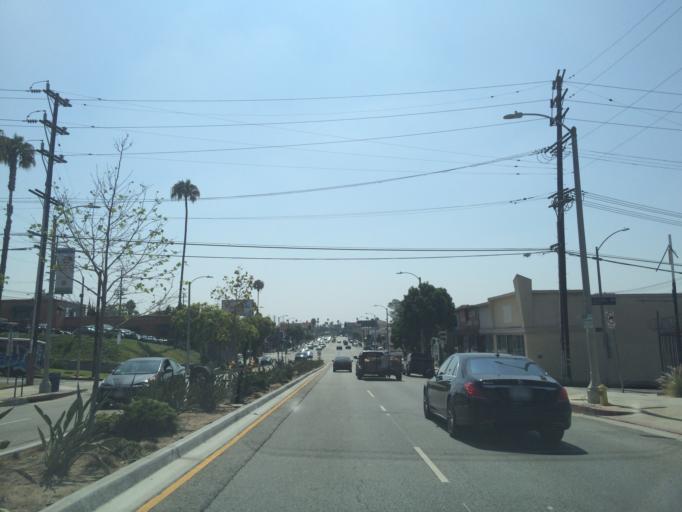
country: US
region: California
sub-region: Los Angeles County
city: West Hollywood
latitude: 34.0504
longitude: -118.3617
